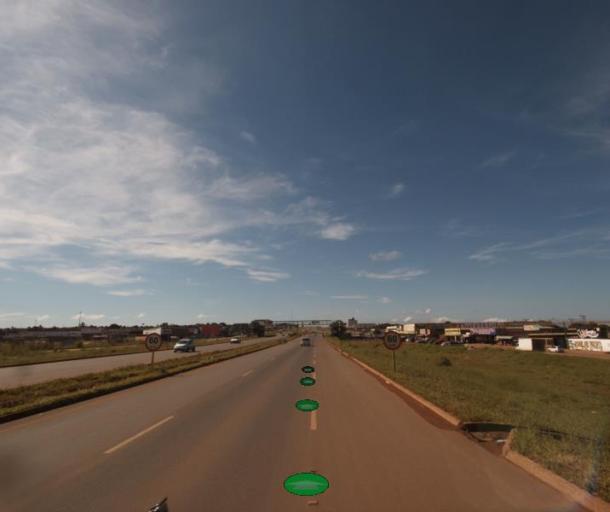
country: BR
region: Federal District
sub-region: Brasilia
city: Brasilia
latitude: -15.7394
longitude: -48.2724
